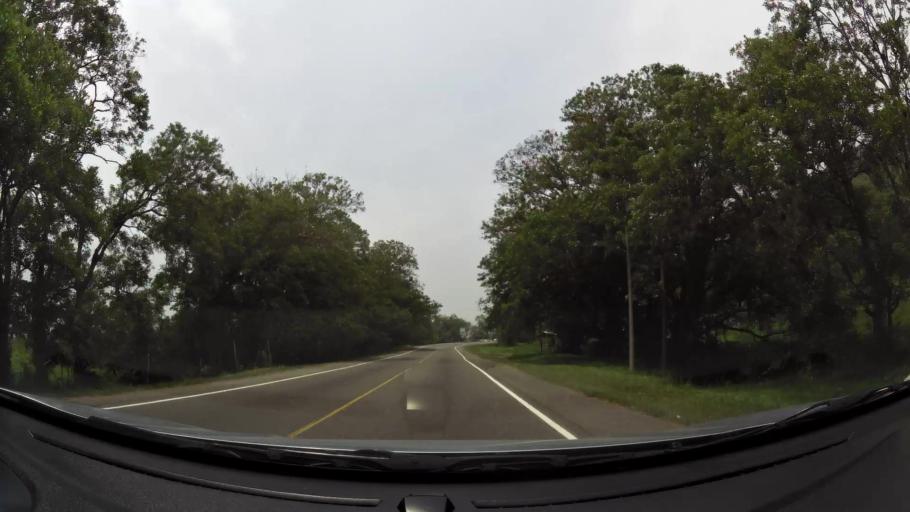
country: HN
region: Cortes
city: La Guama
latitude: 14.8468
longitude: -87.9585
